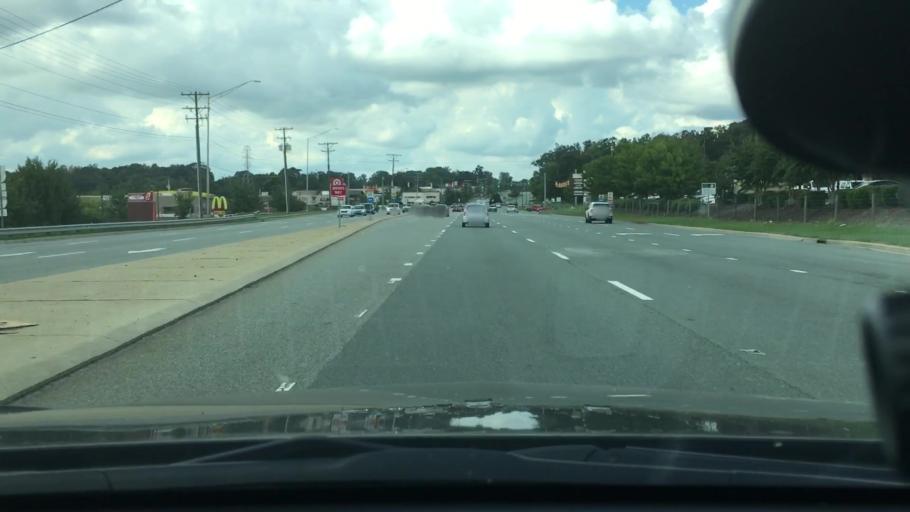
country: US
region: North Carolina
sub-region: Alamance County
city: Elon
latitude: 36.0669
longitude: -79.5178
